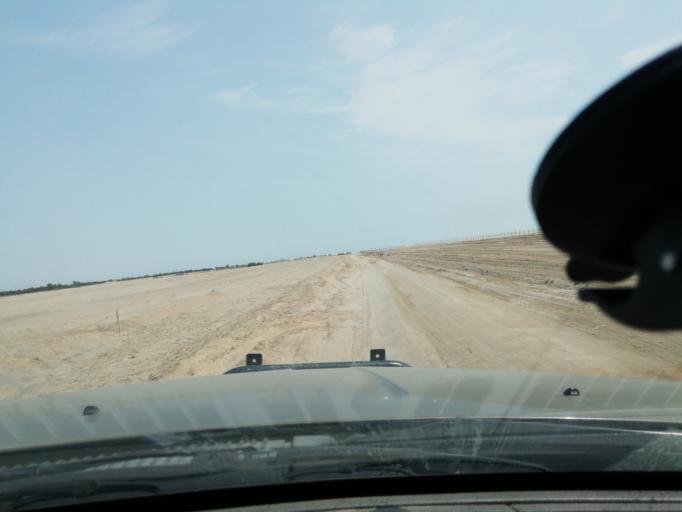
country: PE
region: Ica
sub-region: Provincia de Chincha
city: San Pedro
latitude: -13.3312
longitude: -76.1908
